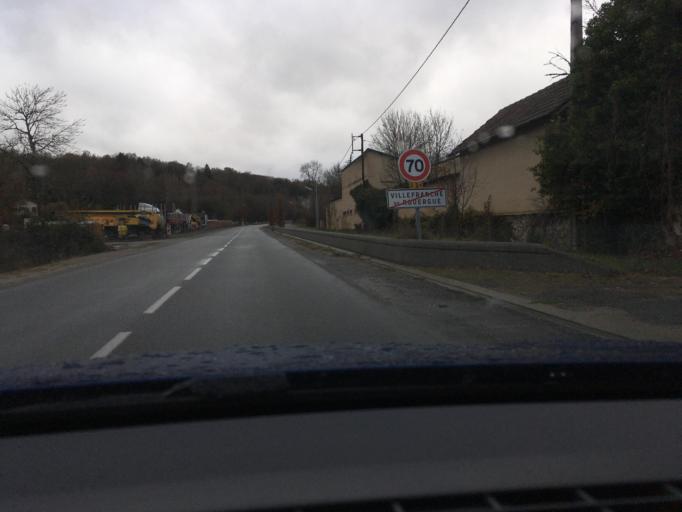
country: FR
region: Midi-Pyrenees
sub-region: Departement de l'Aveyron
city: Villefranche-de-Rouergue
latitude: 44.3648
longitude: 2.0178
